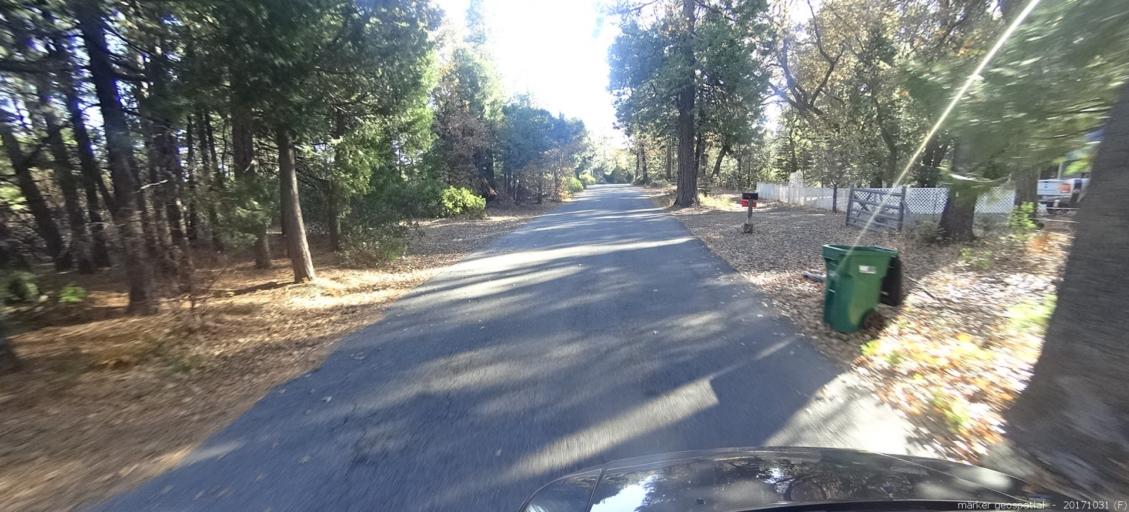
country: US
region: California
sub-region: Shasta County
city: Shingletown
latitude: 40.5179
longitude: -121.8259
